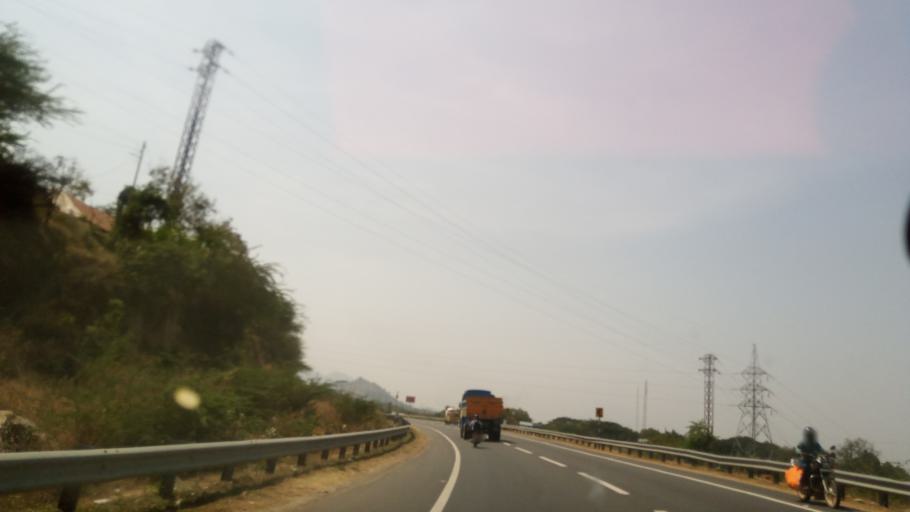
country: IN
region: Tamil Nadu
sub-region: Salem
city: Salem
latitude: 11.6603
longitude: 78.2084
